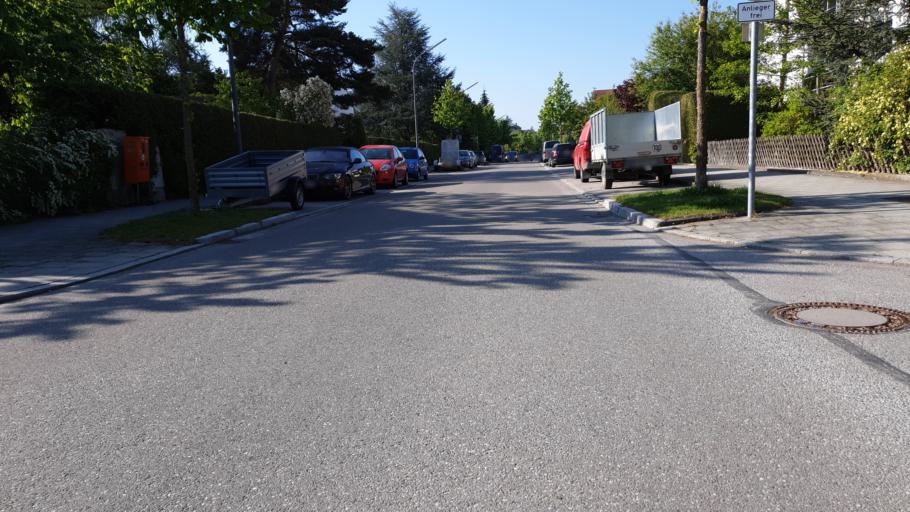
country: DE
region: Bavaria
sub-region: Upper Bavaria
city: Pasing
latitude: 48.1711
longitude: 11.4646
